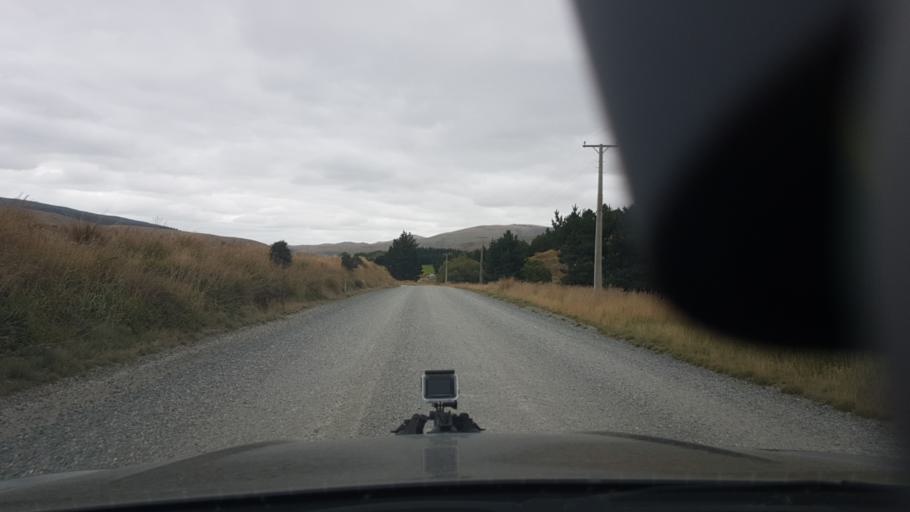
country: NZ
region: Otago
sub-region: Clutha District
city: Papatowai
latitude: -46.2972
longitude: 169.3727
